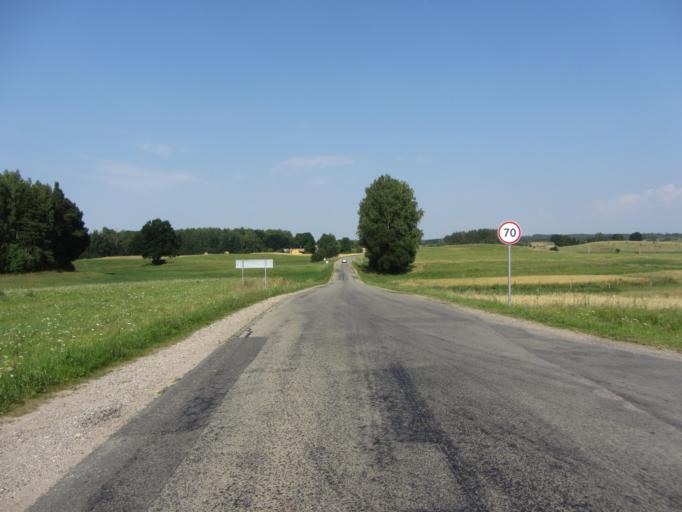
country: LT
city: Veisiejai
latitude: 54.1848
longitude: 23.7266
